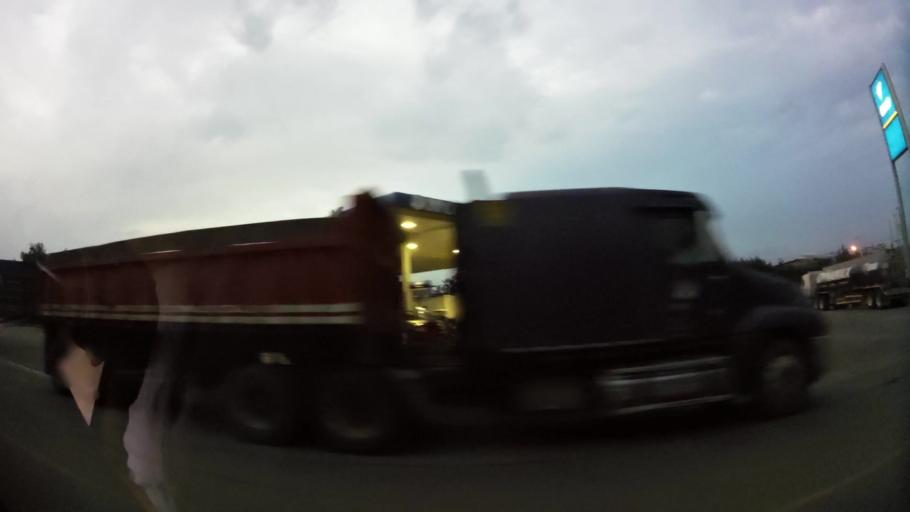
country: NI
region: Esteli
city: Esteli
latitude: 13.1032
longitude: -86.3530
